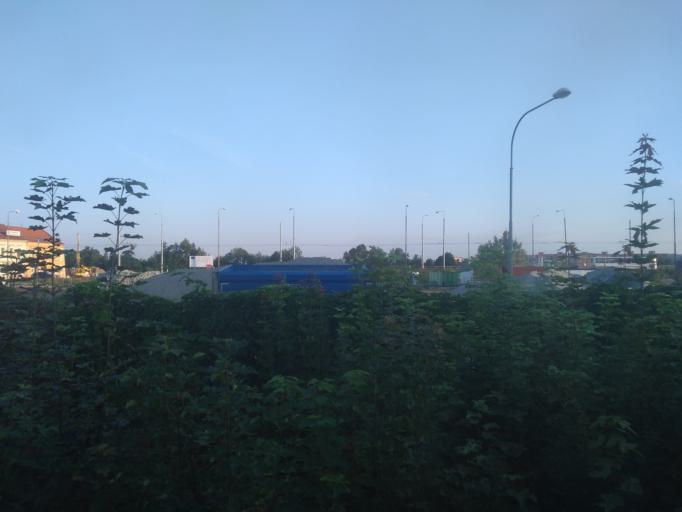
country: CZ
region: Plzensky
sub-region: Okres Plzen-Mesto
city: Pilsen
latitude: 49.7419
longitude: 13.3475
